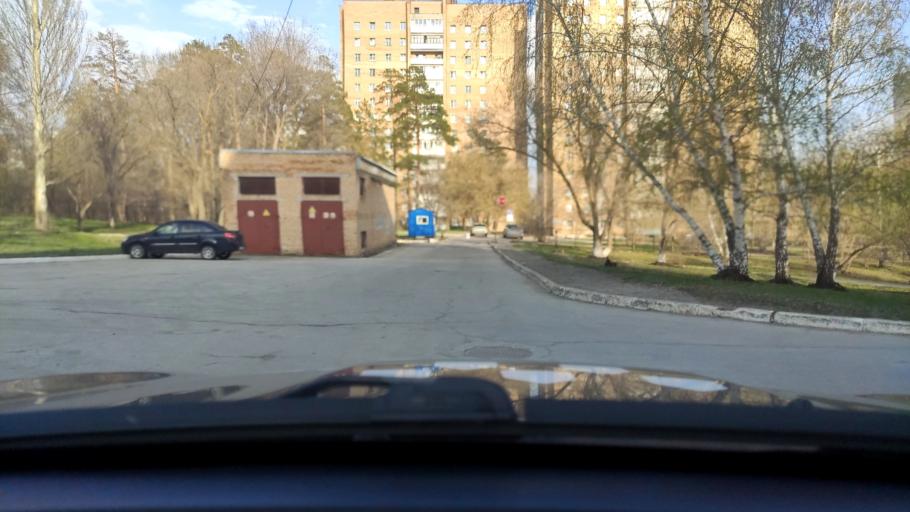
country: RU
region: Samara
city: Zhigulevsk
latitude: 53.4847
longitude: 49.4595
